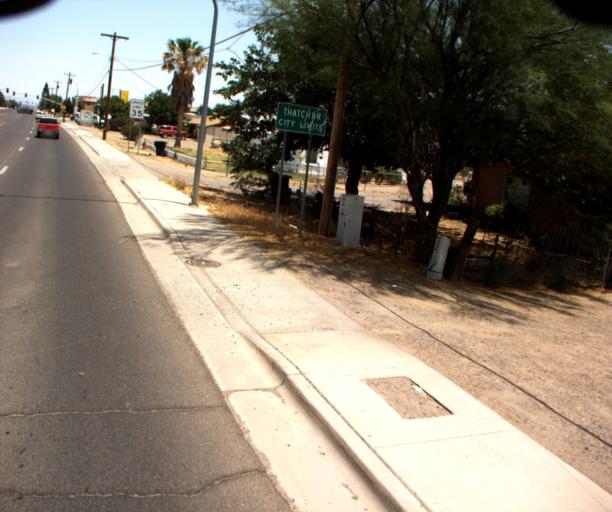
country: US
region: Arizona
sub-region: Graham County
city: Thatcher
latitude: 32.8491
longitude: -109.7693
